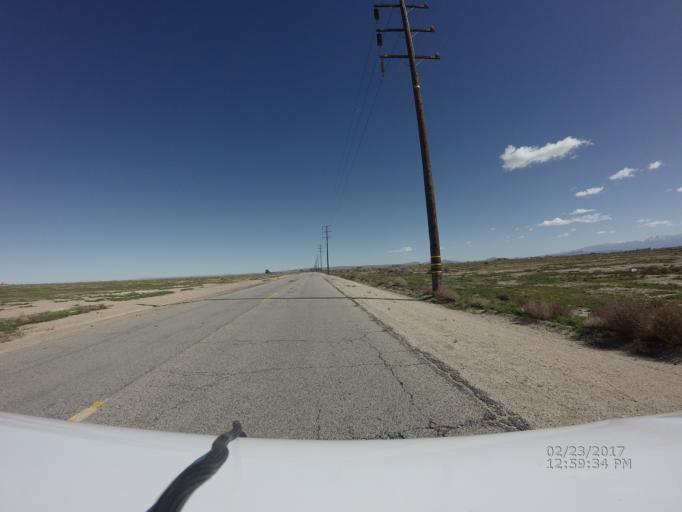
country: US
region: California
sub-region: Los Angeles County
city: Lancaster
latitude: 34.7630
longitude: -118.0341
